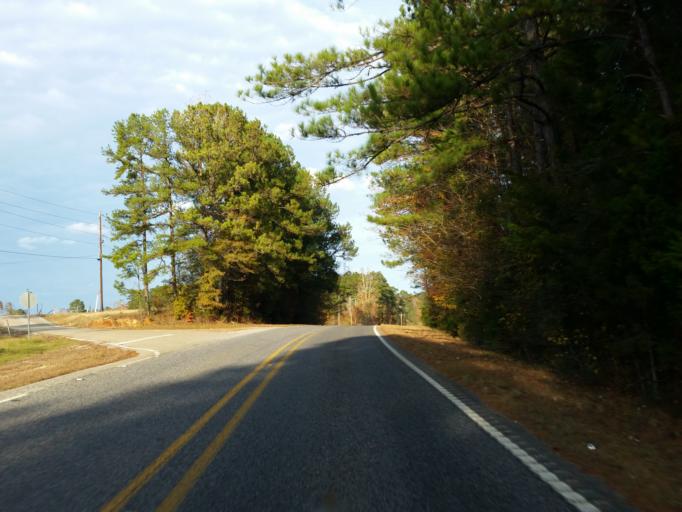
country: US
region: Mississippi
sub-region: Clarke County
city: Stonewall
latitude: 32.2100
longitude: -88.7925
